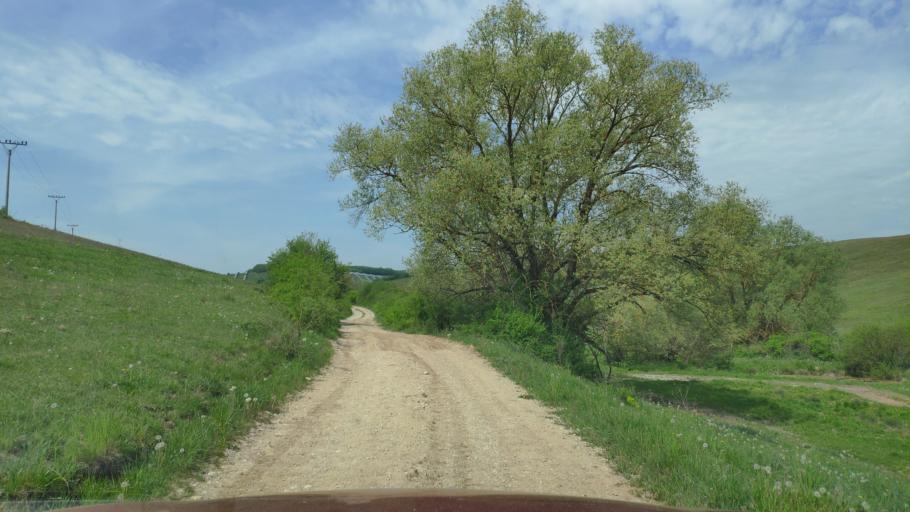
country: SK
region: Banskobystricky
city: Rimavska Sobota
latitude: 48.4302
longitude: 20.1983
